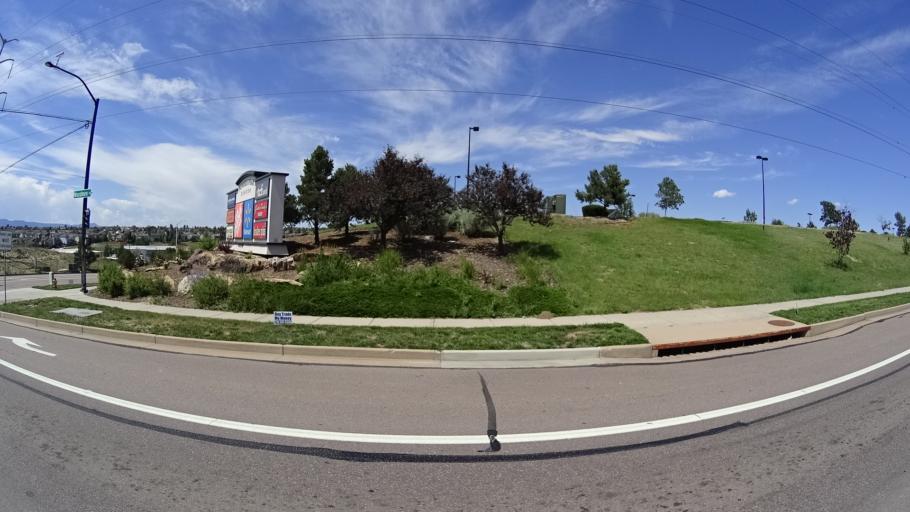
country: US
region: Colorado
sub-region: El Paso County
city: Black Forest
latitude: 38.9402
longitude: -104.7289
